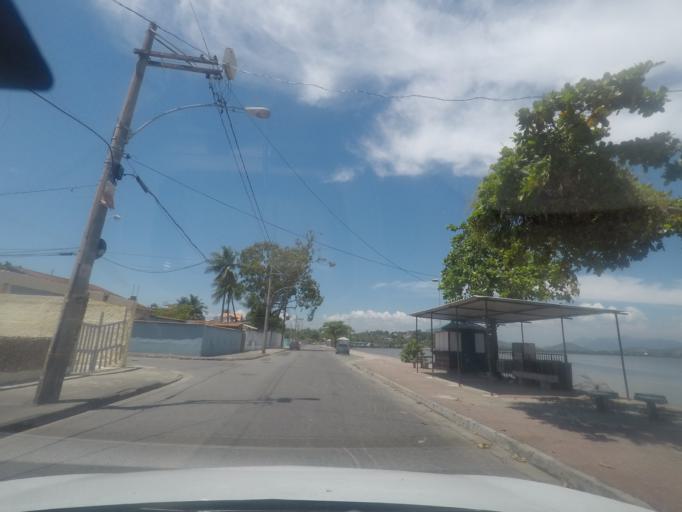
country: BR
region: Rio de Janeiro
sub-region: Itaguai
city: Itaguai
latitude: -22.9878
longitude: -43.6888
